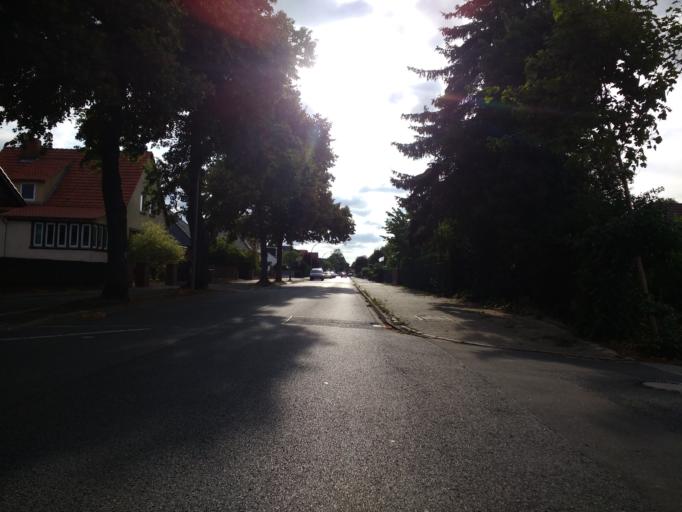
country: DE
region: Lower Saxony
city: Weyhausen
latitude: 52.4210
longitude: 10.7060
